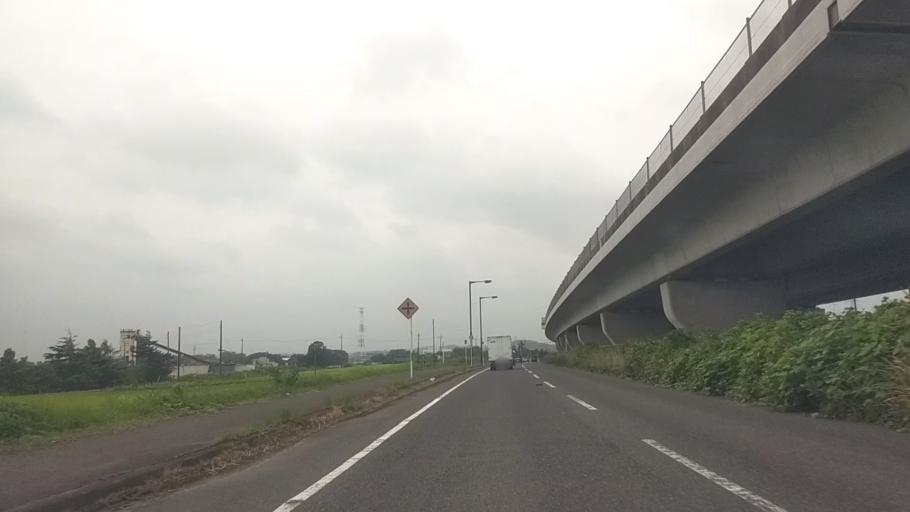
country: JP
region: Chiba
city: Kisarazu
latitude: 35.4060
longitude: 139.9643
